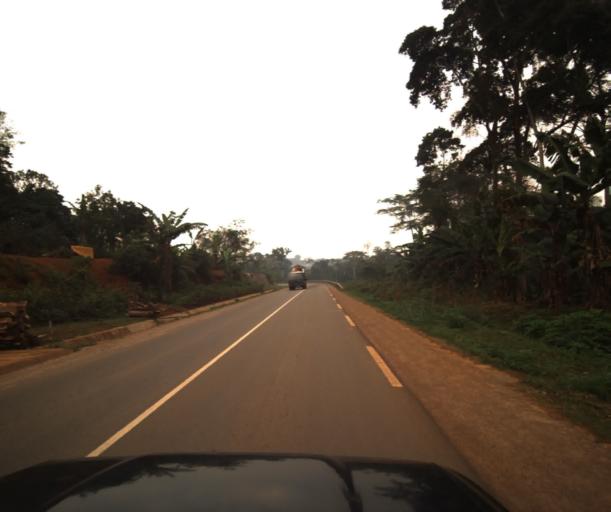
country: CM
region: Centre
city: Mbankomo
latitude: 3.7916
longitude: 11.4491
